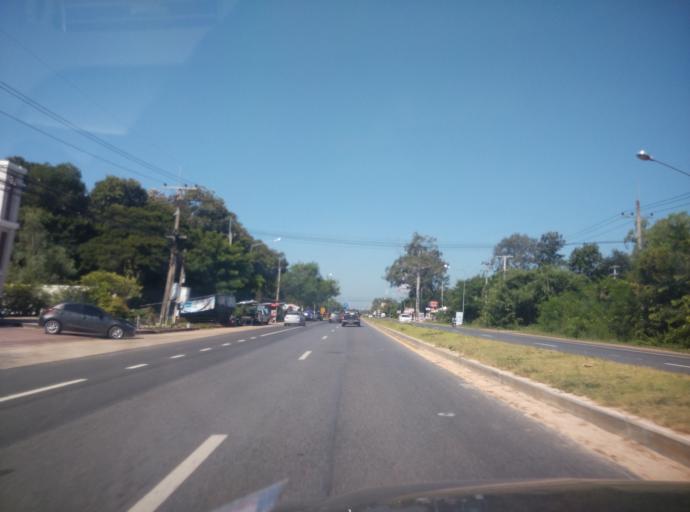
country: TH
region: Sisaket
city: Si Sa Ket
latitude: 15.1248
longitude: 104.2928
